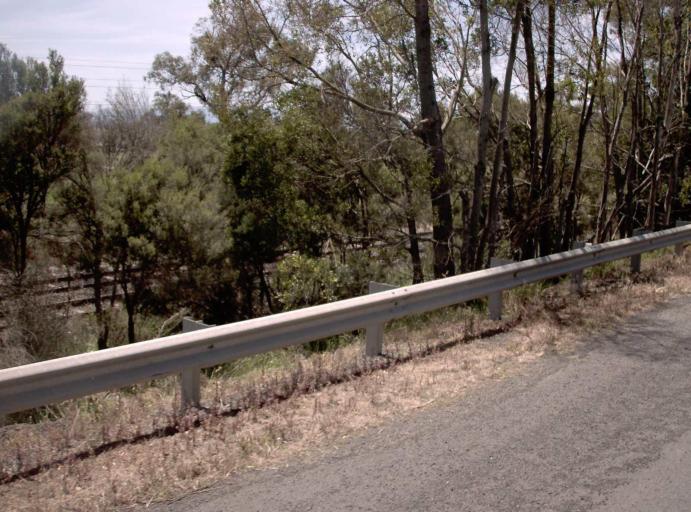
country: AU
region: Victoria
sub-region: Latrobe
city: Moe
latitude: -38.1987
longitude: 146.1964
